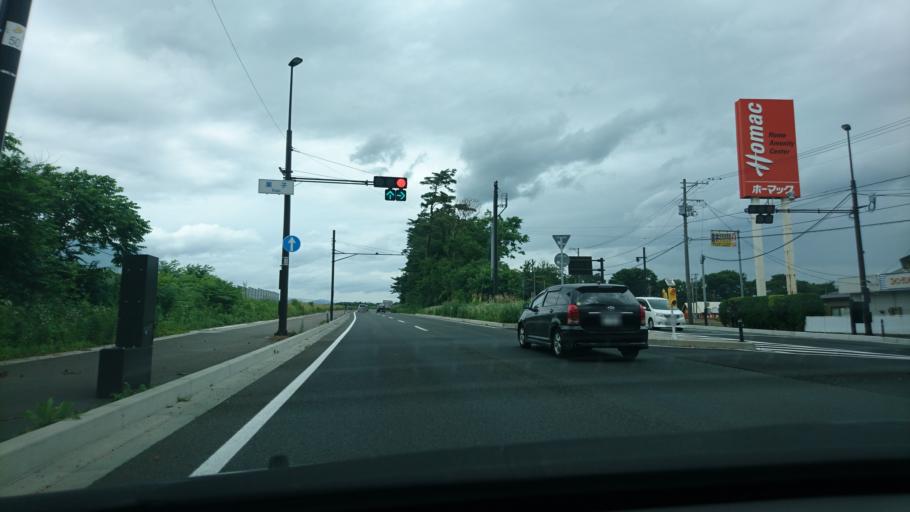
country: JP
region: Iwate
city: Morioka-shi
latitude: 39.7741
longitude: 141.1277
